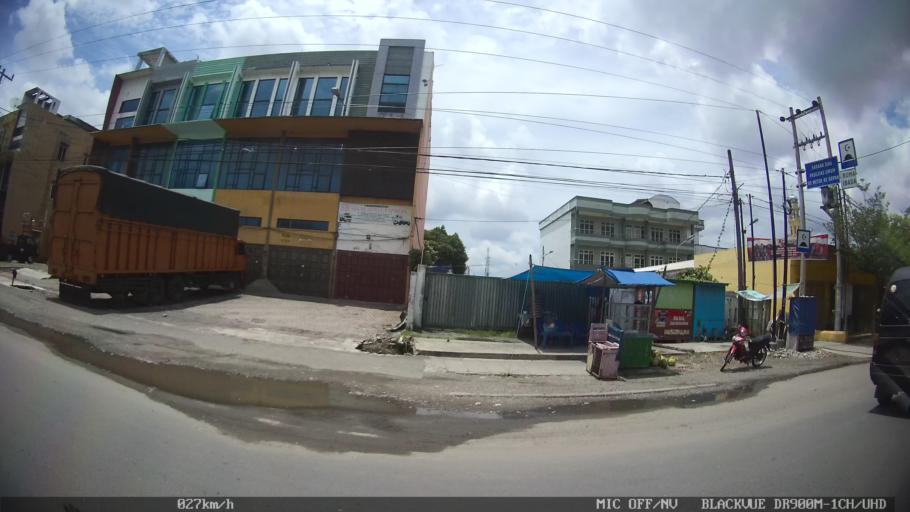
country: ID
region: North Sumatra
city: Medan
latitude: 3.5972
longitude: 98.7254
